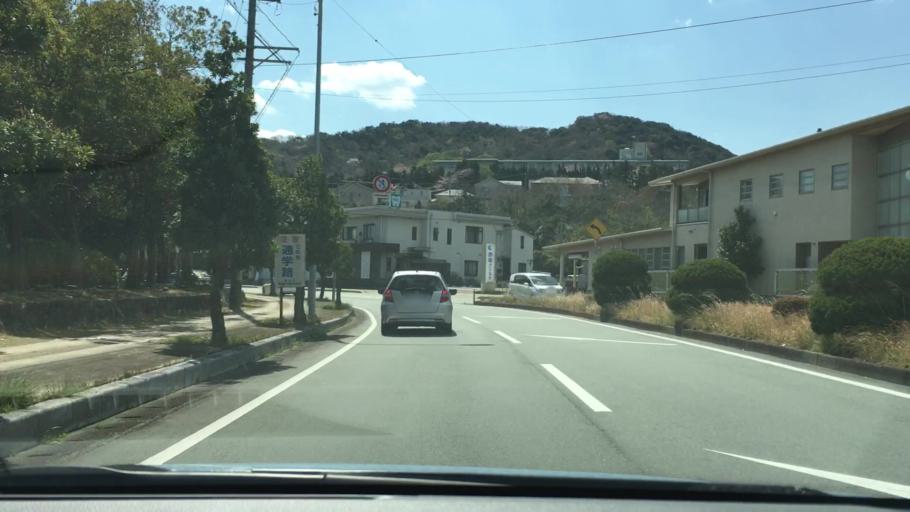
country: JP
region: Mie
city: Toba
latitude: 34.4682
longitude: 136.8490
